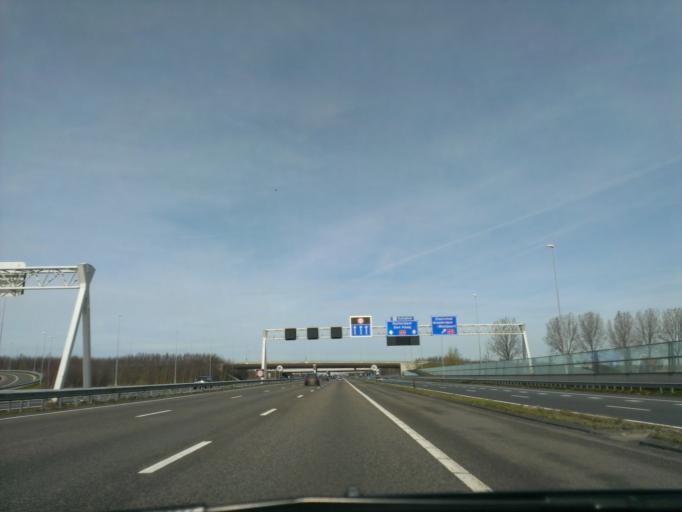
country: NL
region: North Holland
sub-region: Gemeente Haarlemmermeer
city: Hoofddorp
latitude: 52.3540
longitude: 4.7458
